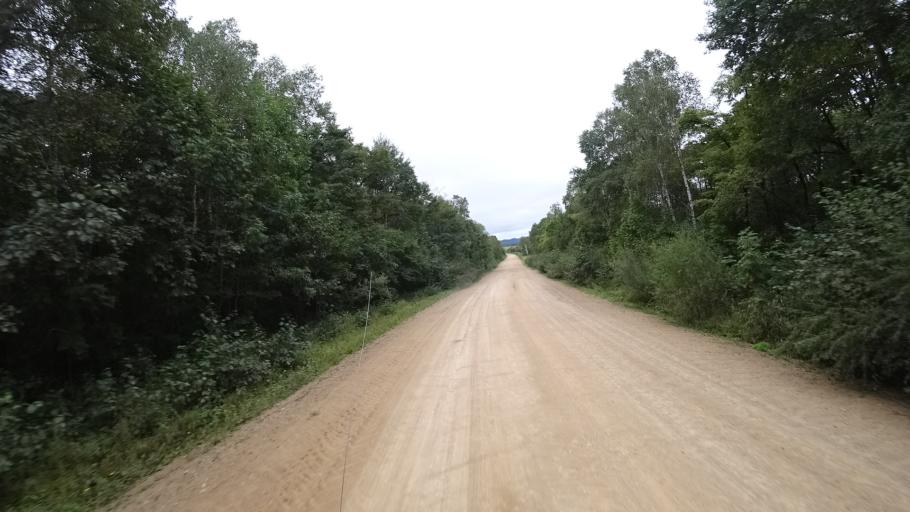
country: RU
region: Primorskiy
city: Rettikhovka
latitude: 44.1619
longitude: 132.7271
